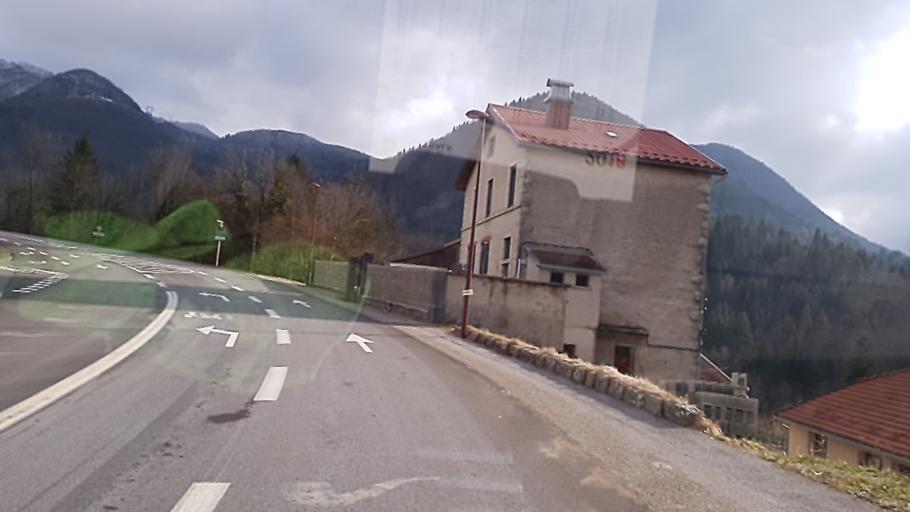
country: FR
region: Franche-Comte
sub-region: Departement du Jura
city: Saint-Claude
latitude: 46.3698
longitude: 5.8748
